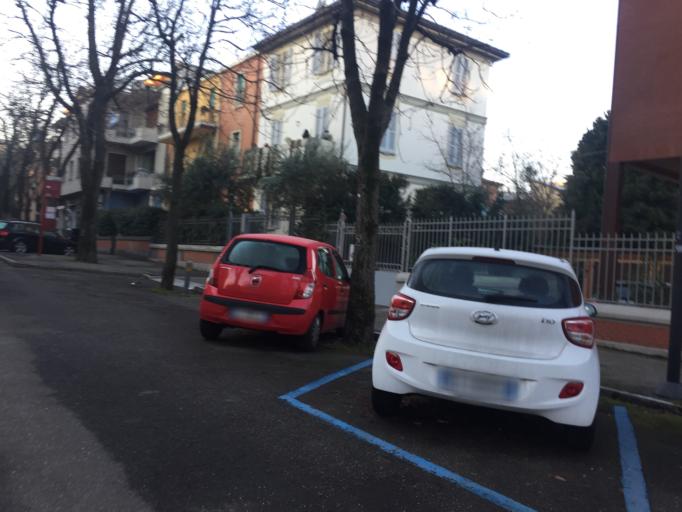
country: IT
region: Emilia-Romagna
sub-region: Provincia di Bologna
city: Bologna
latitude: 44.4931
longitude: 11.3255
